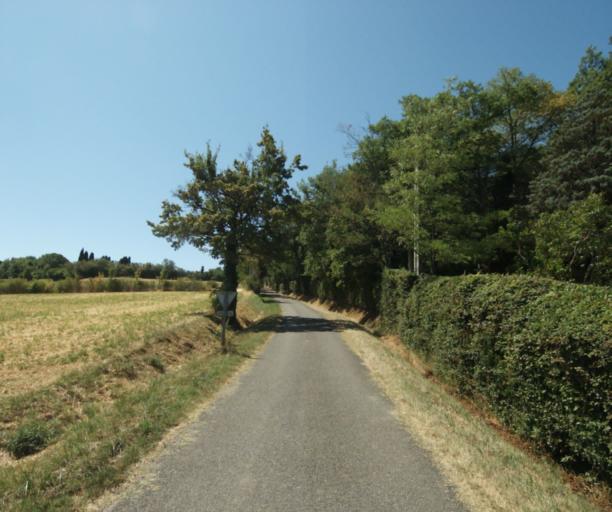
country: FR
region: Midi-Pyrenees
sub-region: Departement de la Haute-Garonne
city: Saint-Felix-Lauragais
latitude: 43.4817
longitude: 1.9243
